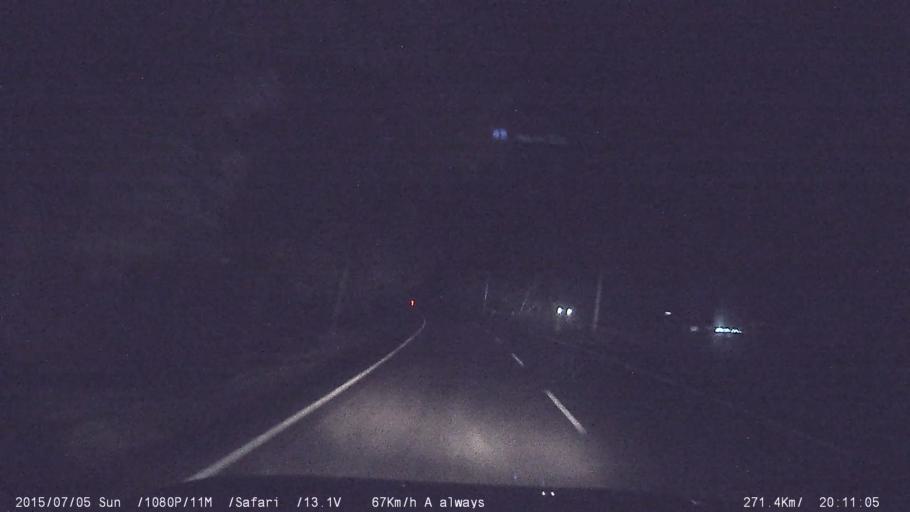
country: IN
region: Kerala
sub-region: Palakkad district
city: Palakkad
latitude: 10.8544
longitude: 76.5731
